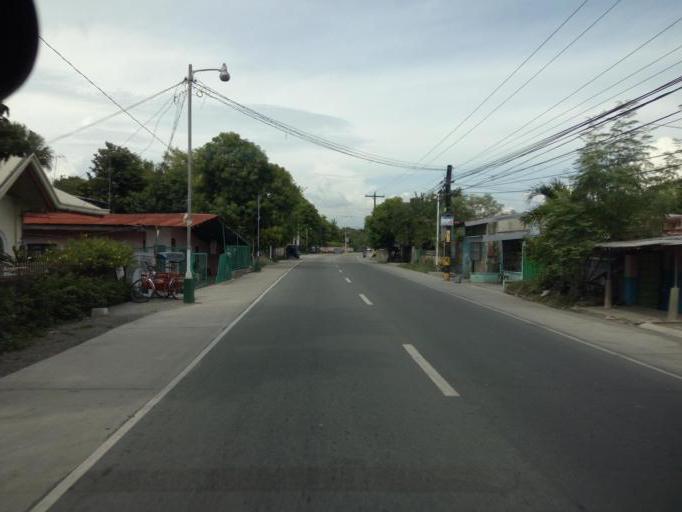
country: PH
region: Ilocos
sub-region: Province of Pangasinan
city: Rosales
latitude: 15.8951
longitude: 120.6396
